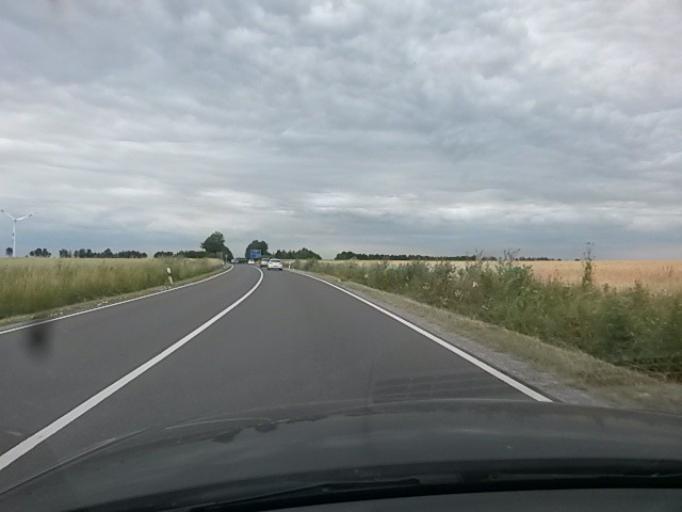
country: DE
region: Bavaria
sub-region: Regierungsbezirk Unterfranken
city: Buchbrunn
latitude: 49.7588
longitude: 10.1149
